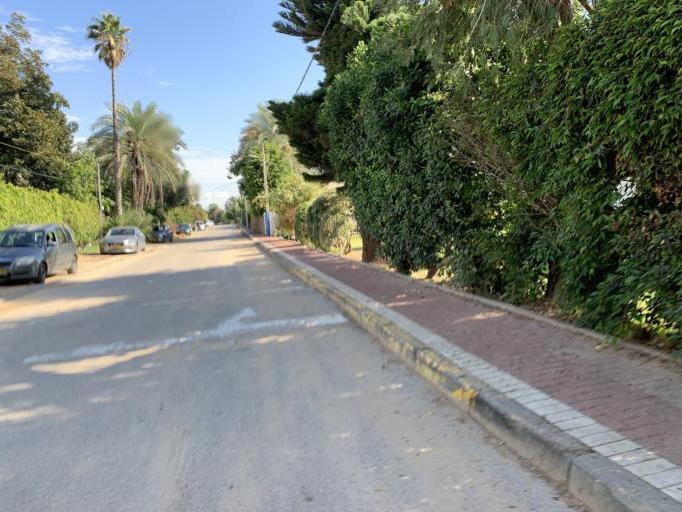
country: IL
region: Central District
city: Ra'anana
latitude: 32.1666
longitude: 34.8704
